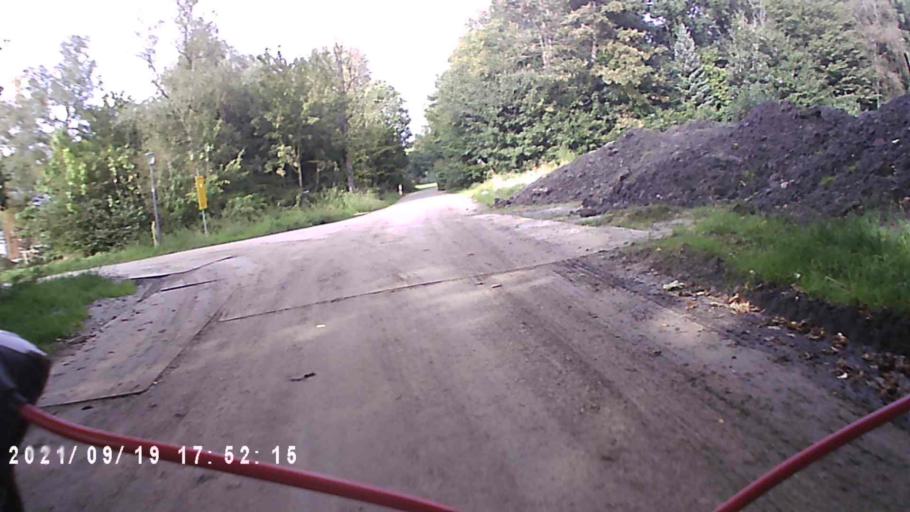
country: NL
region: Groningen
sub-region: Gemeente Delfzijl
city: Delfzijl
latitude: 53.2571
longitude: 6.9417
